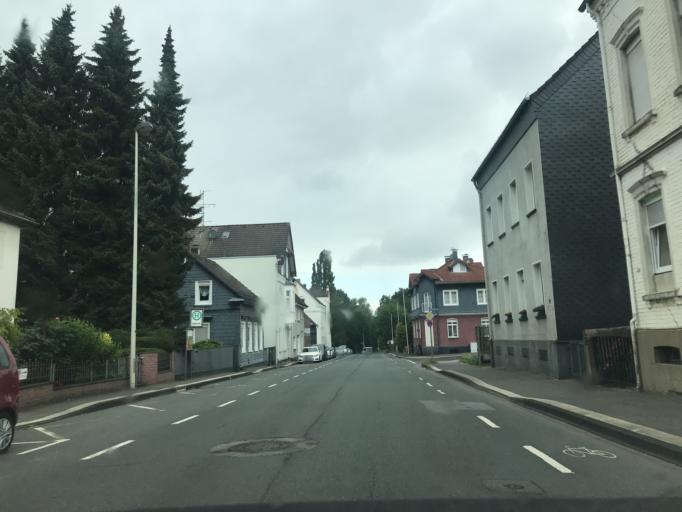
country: DE
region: North Rhine-Westphalia
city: Haan
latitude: 51.1751
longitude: 7.0175
